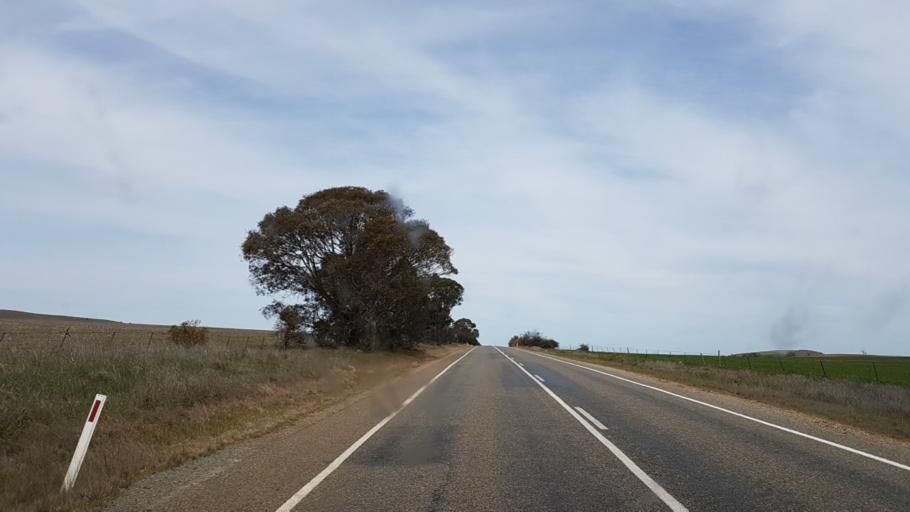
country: AU
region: South Australia
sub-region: Northern Areas
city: Jamestown
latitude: -33.1038
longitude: 138.6194
